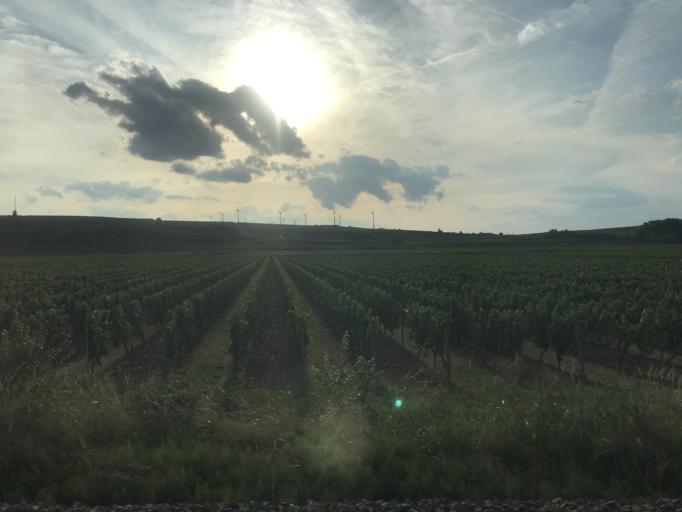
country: DE
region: Rheinland-Pfalz
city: Mettenheim
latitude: 49.7501
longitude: 8.3375
